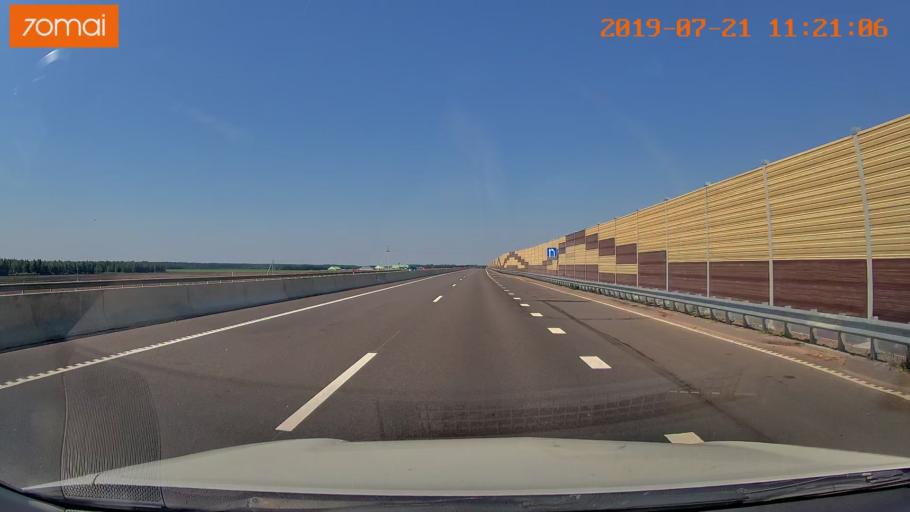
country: BY
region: Minsk
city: Valozhyn
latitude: 54.0388
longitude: 26.6276
